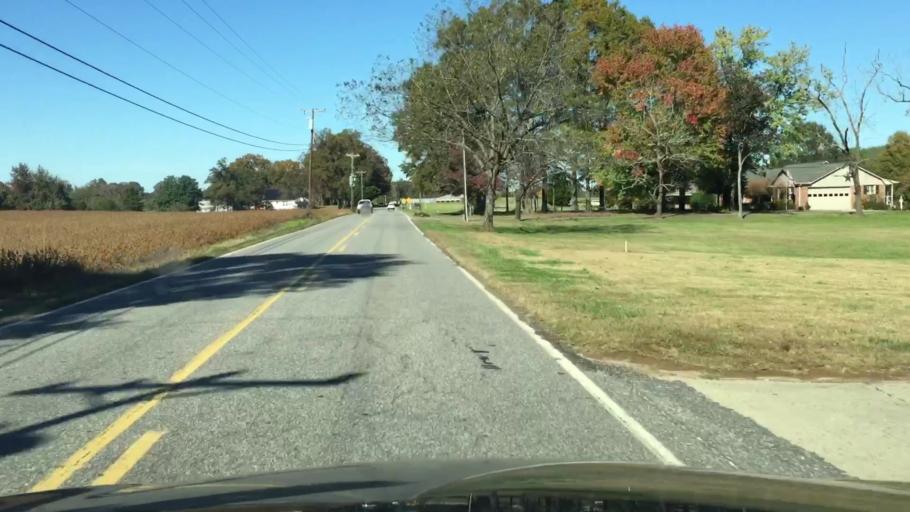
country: US
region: North Carolina
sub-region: Iredell County
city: Mooresville
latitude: 35.5626
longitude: -80.7750
